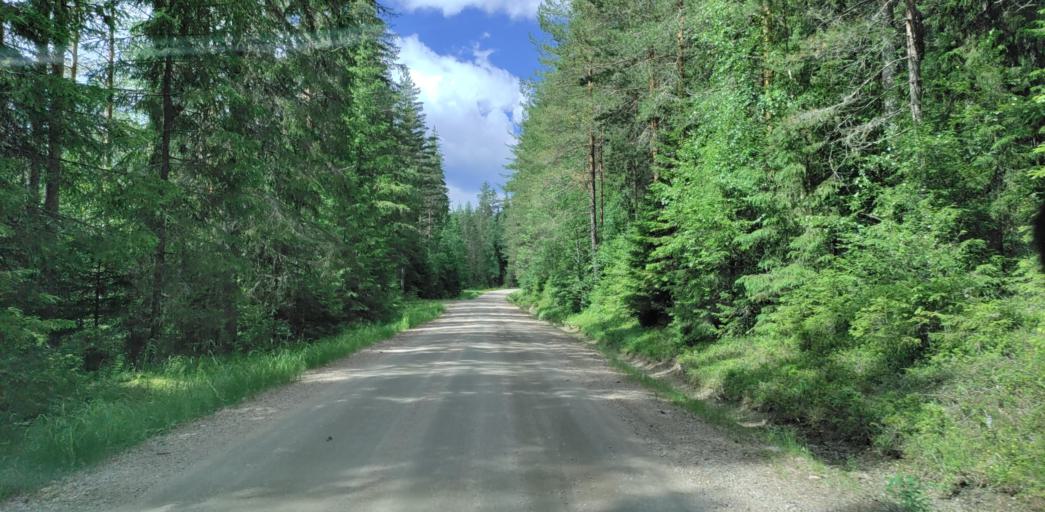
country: SE
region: Vaermland
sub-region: Hagfors Kommun
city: Ekshaerad
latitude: 60.0976
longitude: 13.3966
